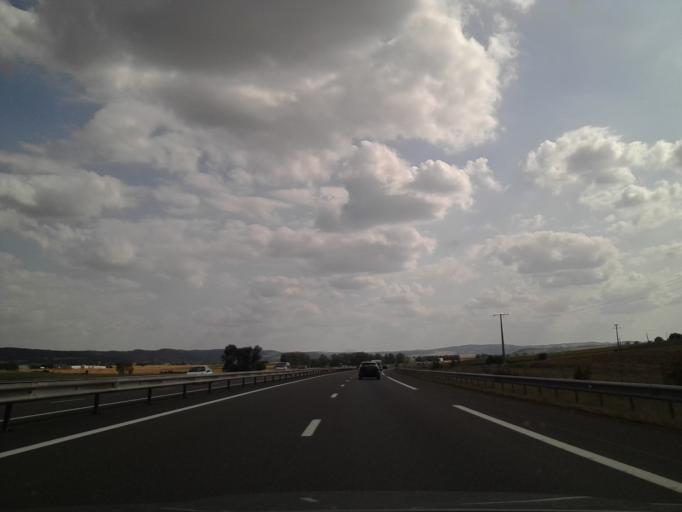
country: FR
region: Auvergne
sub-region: Departement de l'Allier
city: Bellenaves
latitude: 46.1640
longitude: 3.1294
